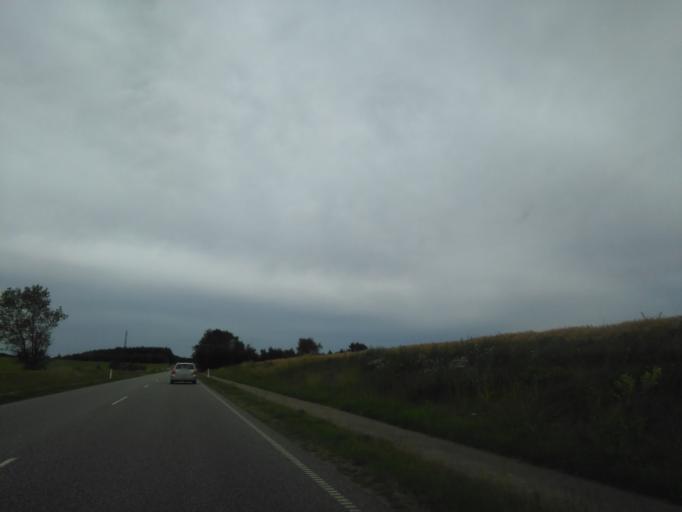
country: DK
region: Central Jutland
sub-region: Horsens Kommune
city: Horsens
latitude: 55.9221
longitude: 9.9373
